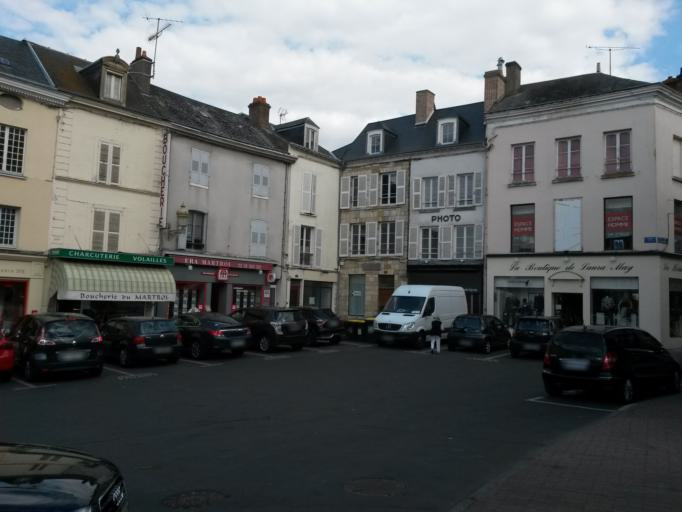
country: FR
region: Centre
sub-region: Departement du Loiret
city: Pithiviers
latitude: 48.1734
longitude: 2.2551
